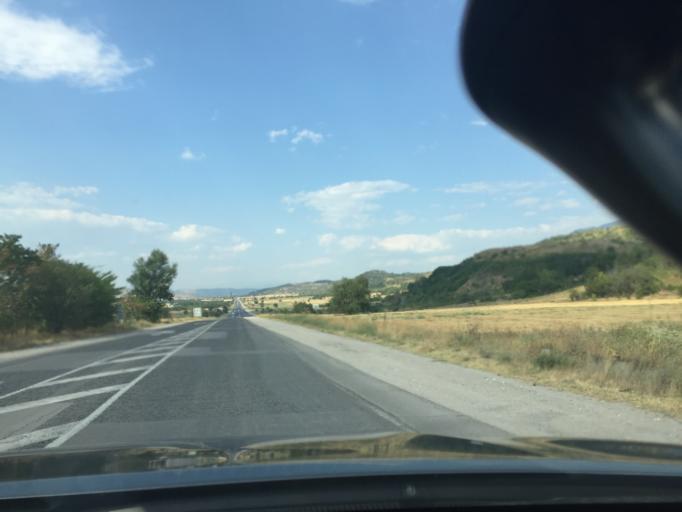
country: BG
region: Kyustendil
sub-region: Obshtina Boboshevo
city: Boboshevo
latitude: 42.1623
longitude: 23.0428
